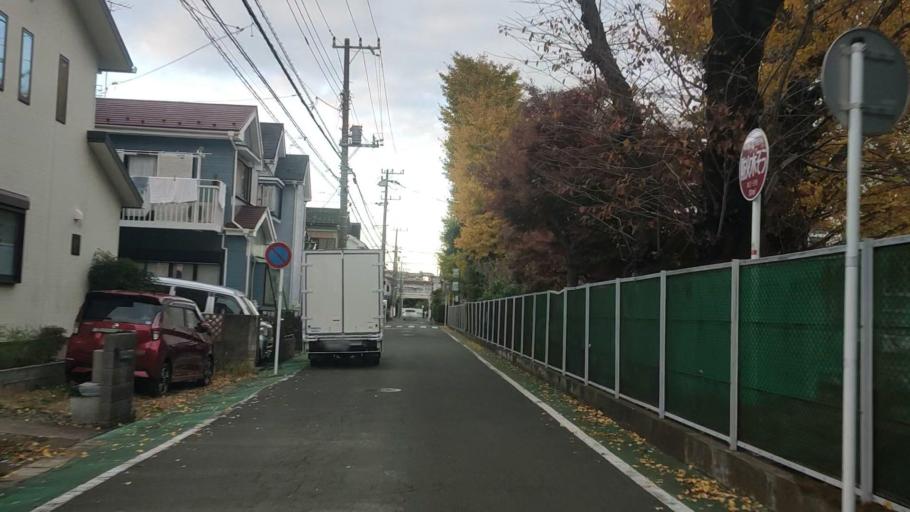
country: JP
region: Kanagawa
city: Minami-rinkan
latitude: 35.4676
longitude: 139.4691
